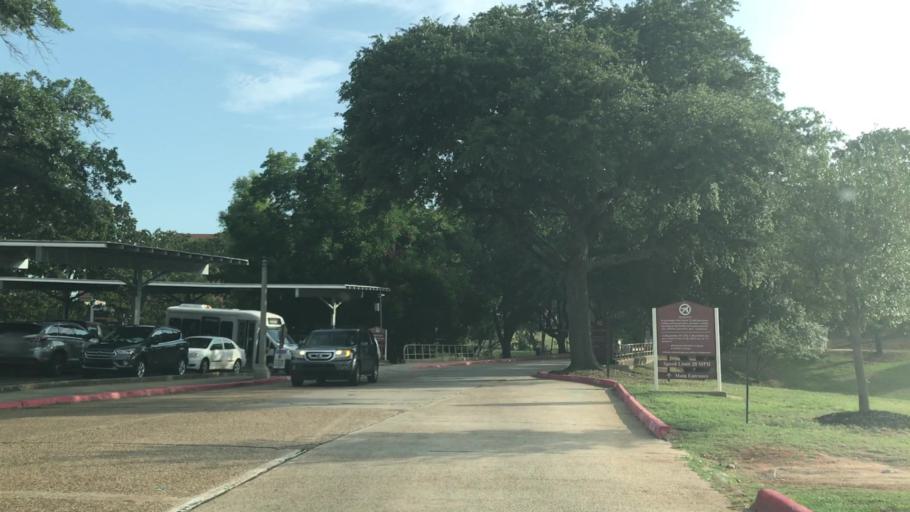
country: US
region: Louisiana
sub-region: Bossier Parish
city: Bossier City
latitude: 32.5002
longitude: -93.7221
